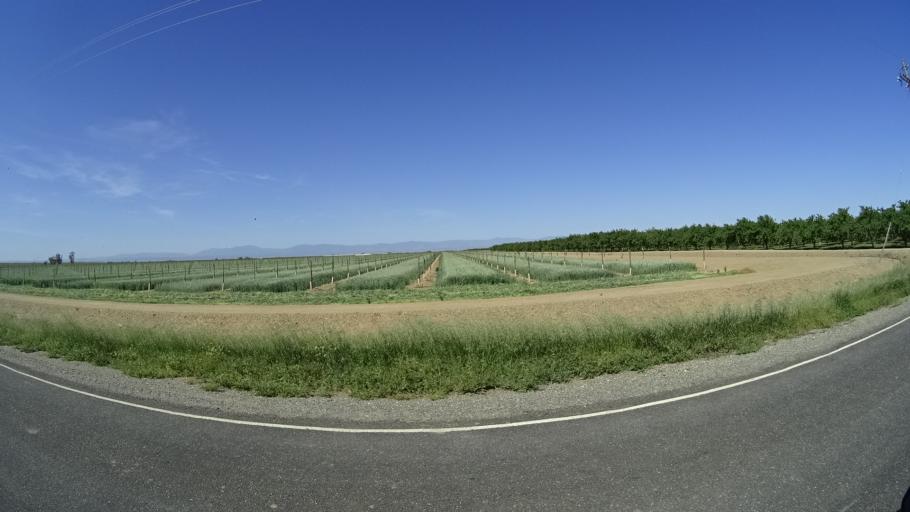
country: US
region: California
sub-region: Glenn County
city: Hamilton City
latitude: 39.6450
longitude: -122.1037
